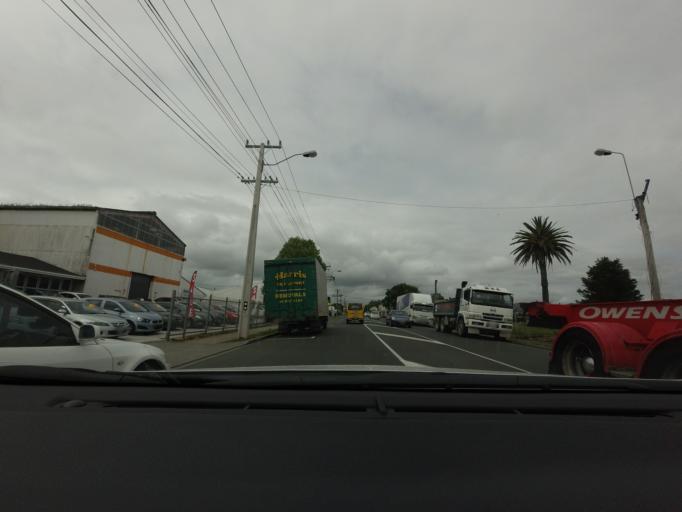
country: NZ
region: Auckland
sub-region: Auckland
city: Rosebank
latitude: -36.8851
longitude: 174.6286
